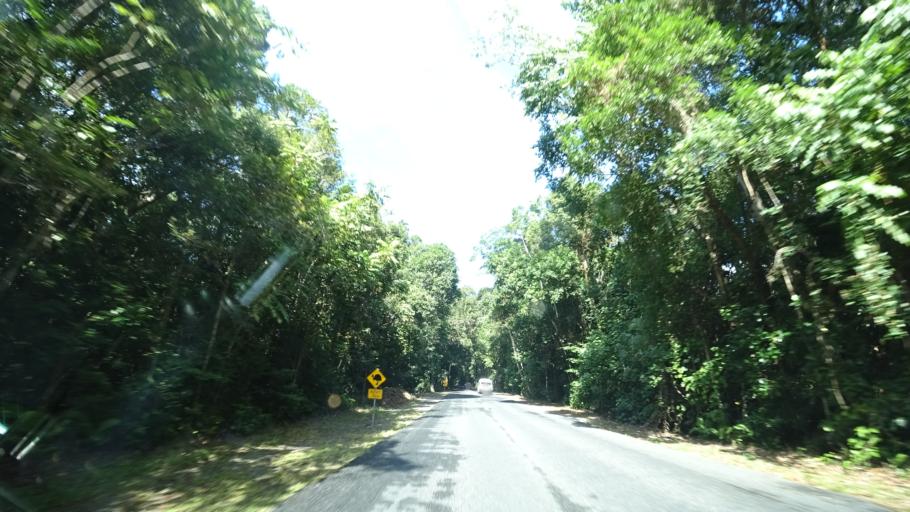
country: AU
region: Queensland
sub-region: Cairns
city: Port Douglas
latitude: -16.1345
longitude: 145.4514
